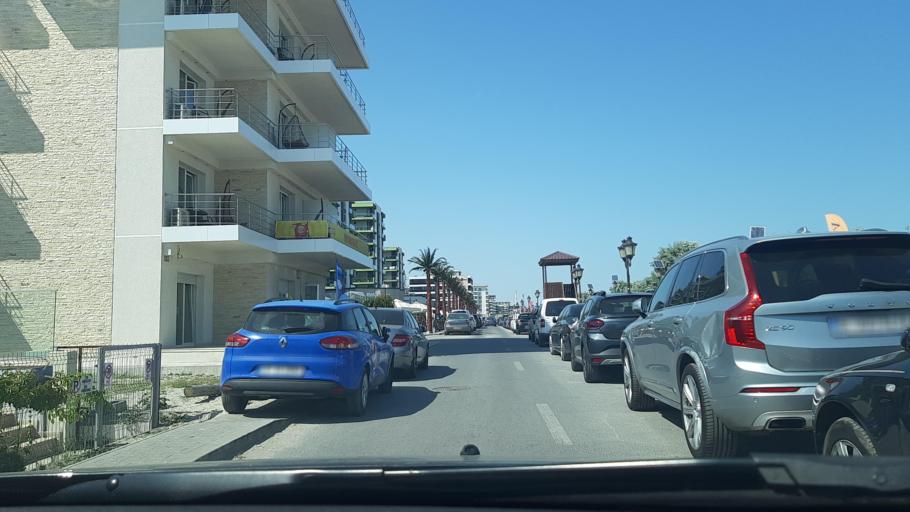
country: RO
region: Constanta
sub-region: Comuna Navodari
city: Navodari
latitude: 44.3000
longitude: 28.6260
